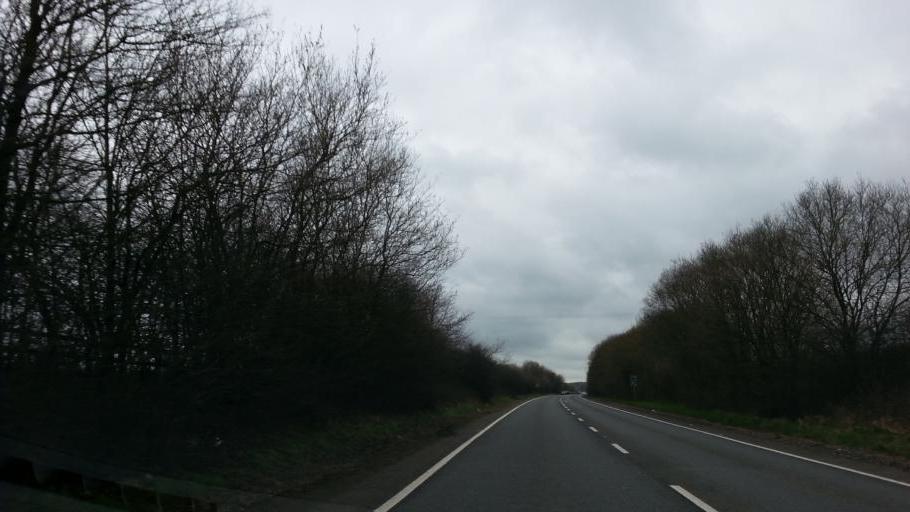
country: GB
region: England
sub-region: Devon
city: South Molton
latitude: 51.0304
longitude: -3.8345
